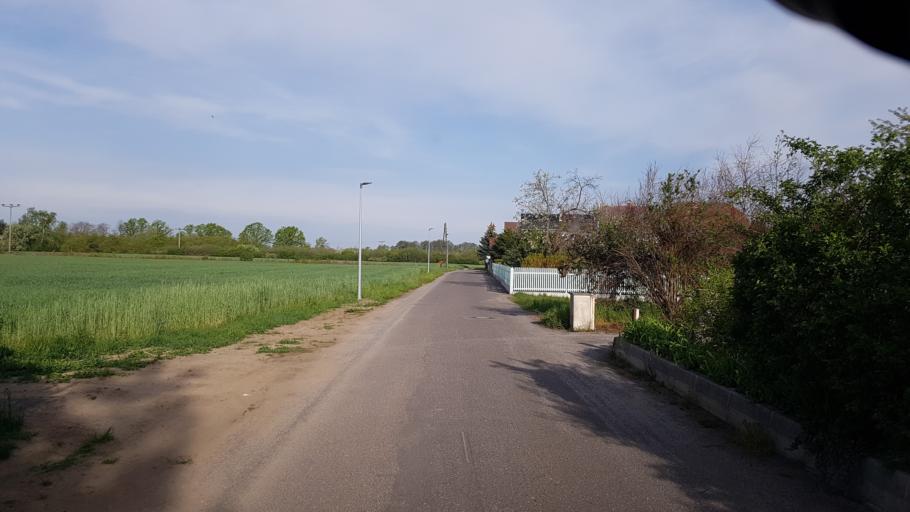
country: DE
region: Brandenburg
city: Ortrand
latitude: 51.3796
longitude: 13.7536
